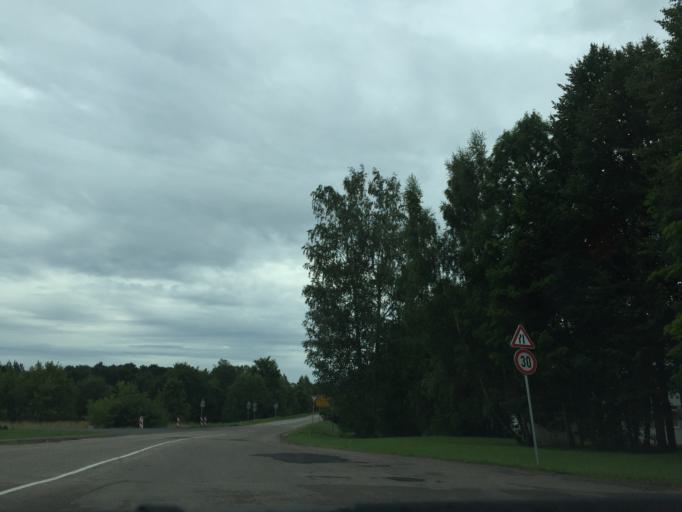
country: LV
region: Preilu Rajons
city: Preili
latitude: 56.2889
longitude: 26.7373
